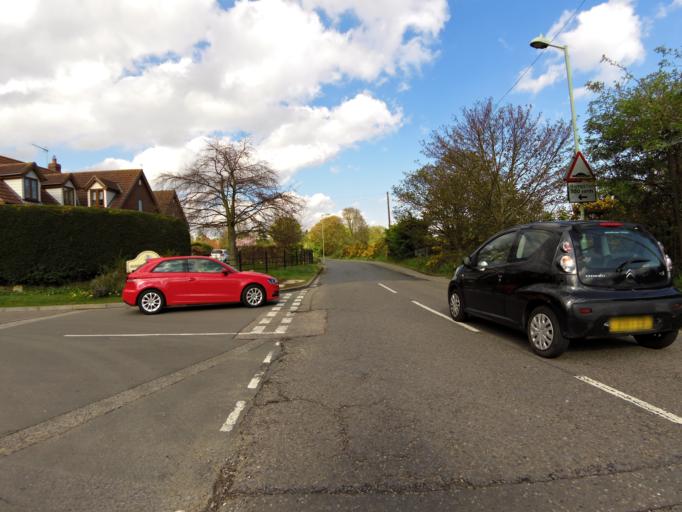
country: GB
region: England
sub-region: Suffolk
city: Kesgrave
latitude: 52.0627
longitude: 1.2053
